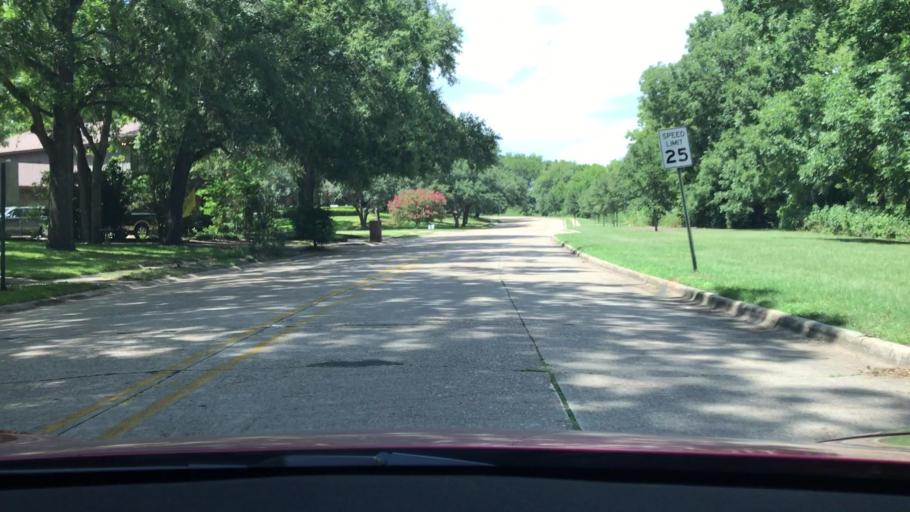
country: US
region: Louisiana
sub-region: Bossier Parish
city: Bossier City
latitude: 32.4316
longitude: -93.7282
